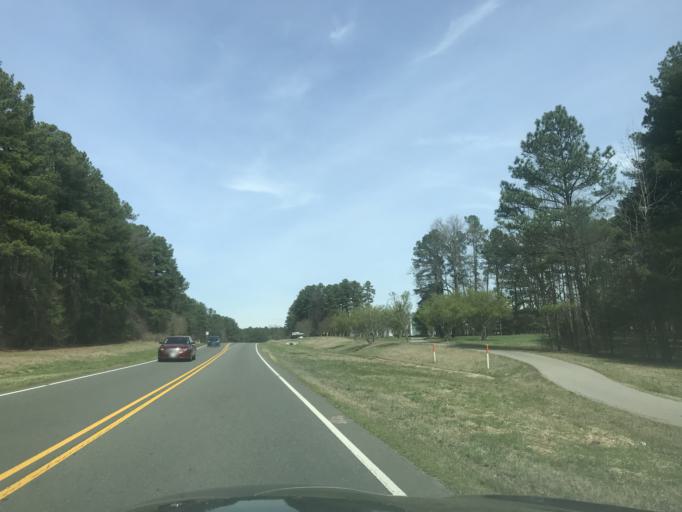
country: US
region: North Carolina
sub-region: Durham County
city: Durham
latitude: 35.9118
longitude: -78.8779
